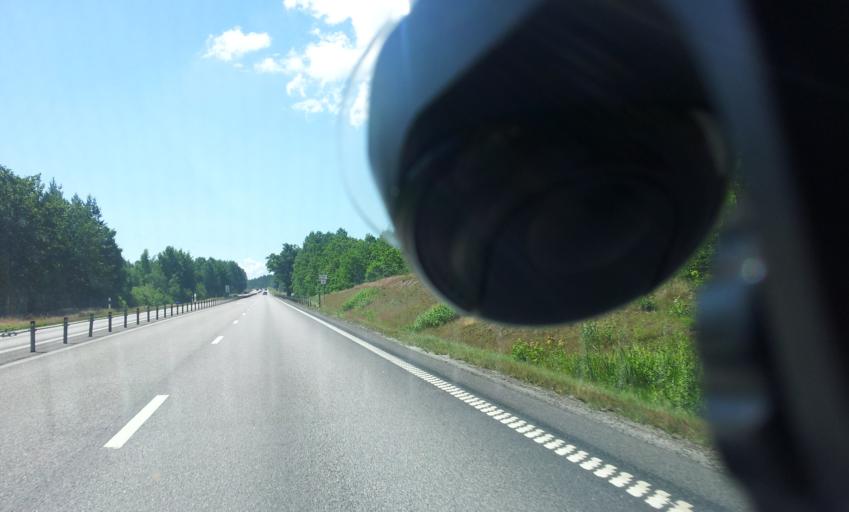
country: SE
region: Kalmar
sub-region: Oskarshamns Kommun
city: Paskallavik
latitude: 57.1444
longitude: 16.4691
